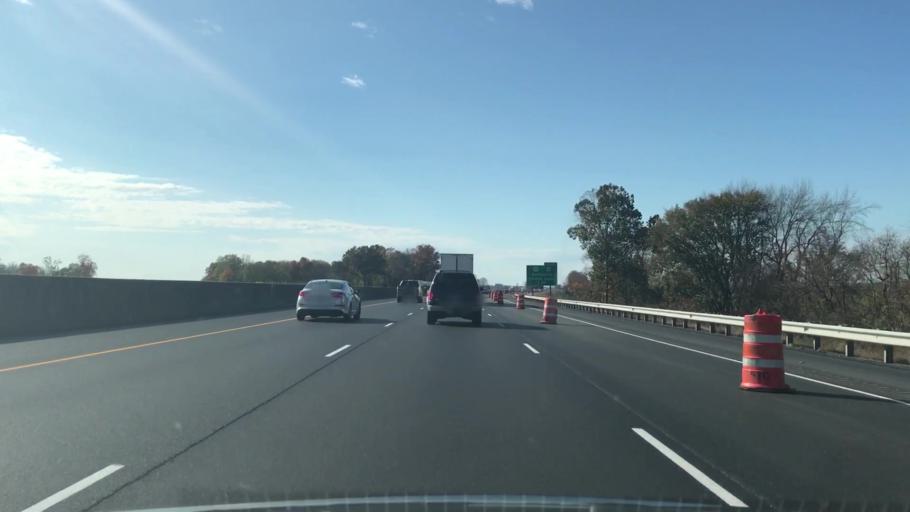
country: US
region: Kentucky
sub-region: Edmonson County
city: Brownsville
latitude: 37.0414
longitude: -86.1839
